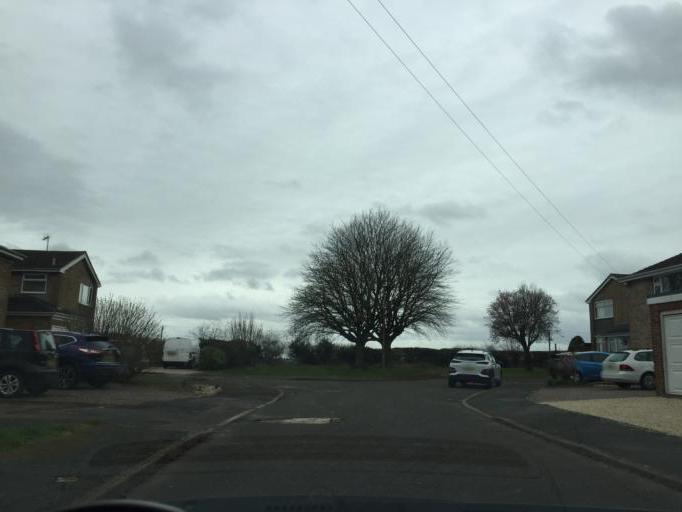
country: GB
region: England
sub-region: Oxfordshire
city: Banbury
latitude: 52.0443
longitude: -1.3369
